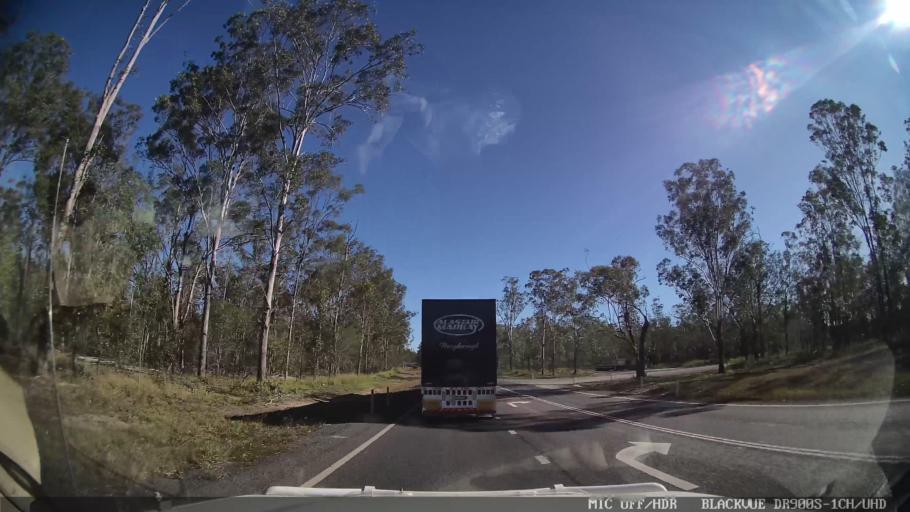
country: AU
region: Queensland
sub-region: Bundaberg
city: Childers
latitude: -25.2114
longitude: 152.0838
